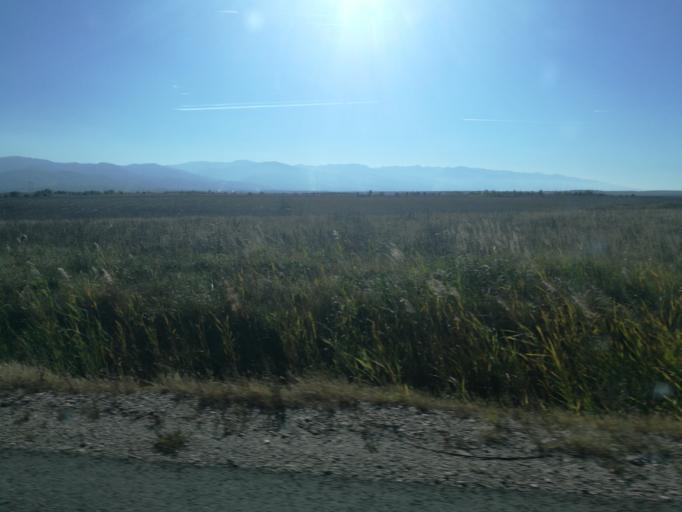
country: RO
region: Brasov
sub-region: Comuna Sinca Veche
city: Sinca Veche
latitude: 45.8080
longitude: 25.1717
